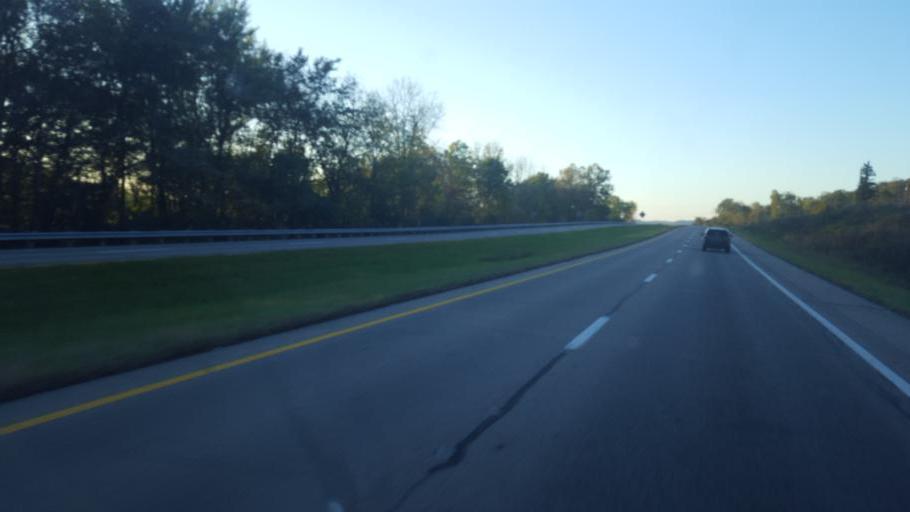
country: US
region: Ohio
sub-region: Scioto County
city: Lucasville
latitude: 38.9130
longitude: -83.0126
